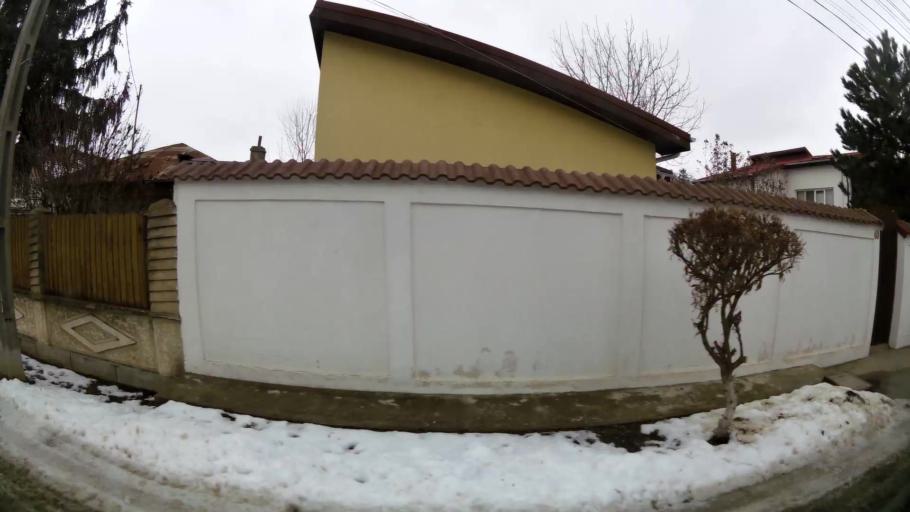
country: RO
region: Ilfov
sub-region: Comuna Tunari
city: Tunari
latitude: 44.5447
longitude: 26.1304
